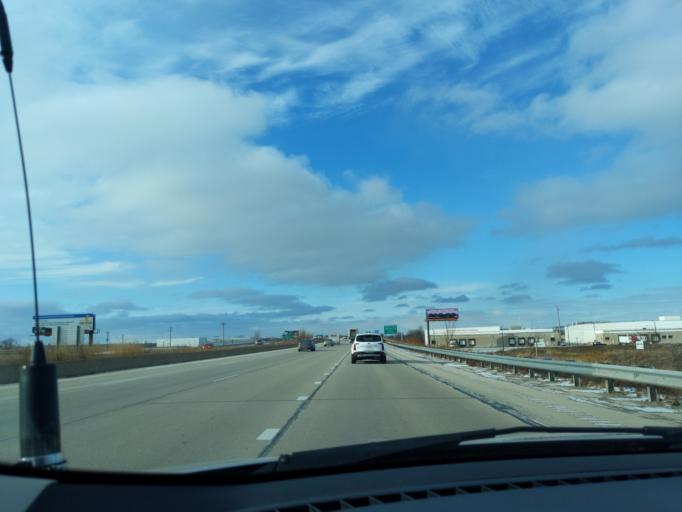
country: US
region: Wisconsin
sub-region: Brown County
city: Ashwaubenon
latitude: 44.4769
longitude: -88.0522
